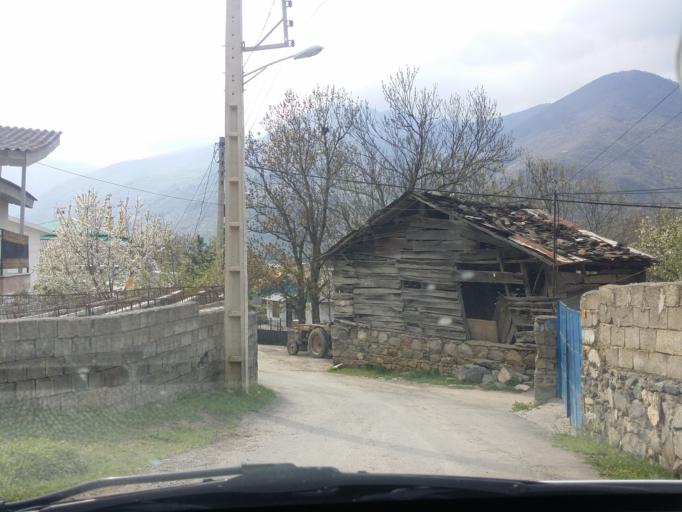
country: IR
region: Mazandaran
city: `Abbasabad
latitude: 36.4826
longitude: 51.1400
